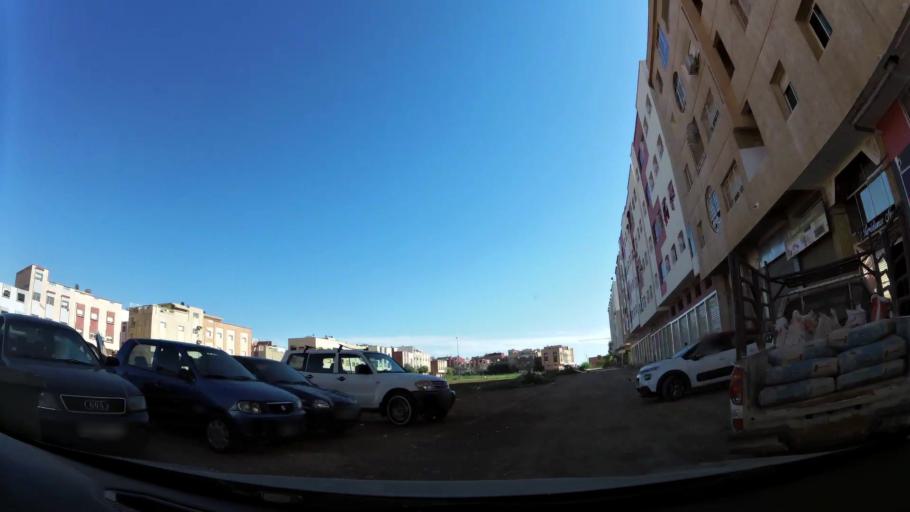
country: MA
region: Meknes-Tafilalet
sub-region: Meknes
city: Meknes
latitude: 33.8786
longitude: -5.5777
